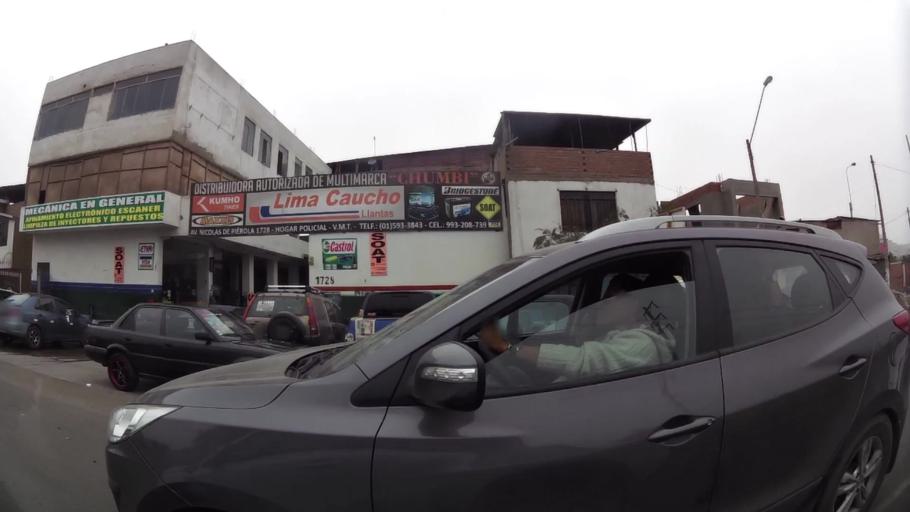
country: PE
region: Lima
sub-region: Lima
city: Surco
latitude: -12.1737
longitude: -76.9439
